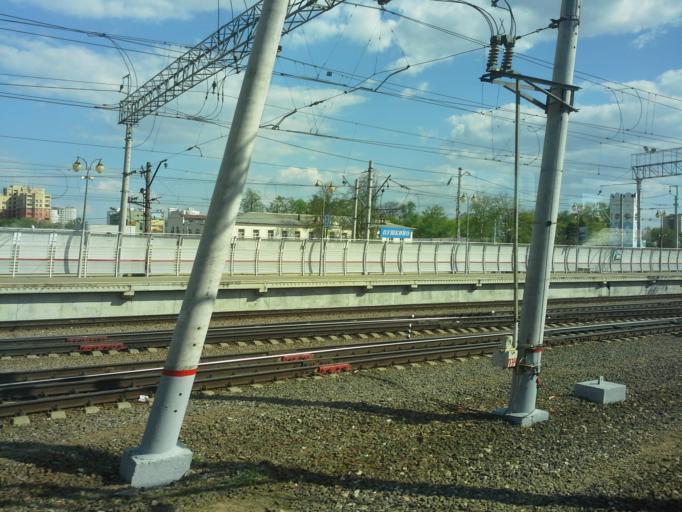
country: RU
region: Moskovskaya
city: Pushkino
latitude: 56.0147
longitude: 37.8403
